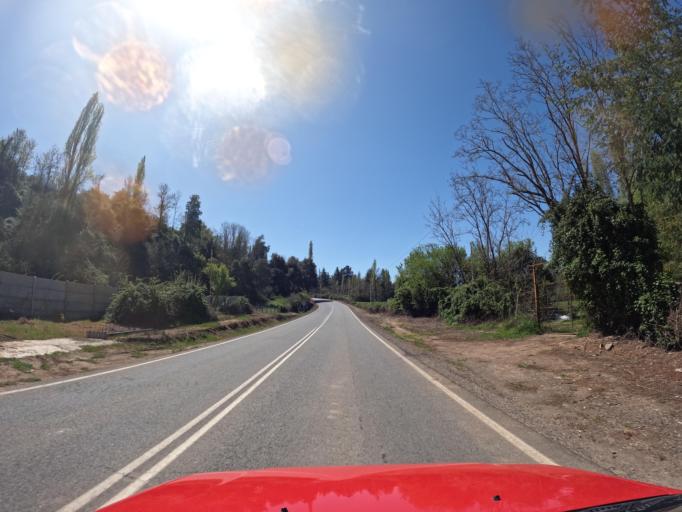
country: CL
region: Maule
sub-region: Provincia de Talca
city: San Clemente
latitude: -35.4569
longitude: -71.2693
